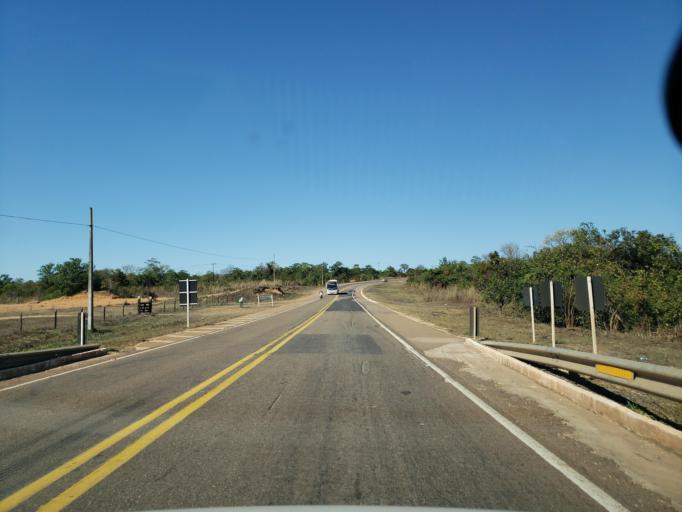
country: BR
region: Mato Grosso
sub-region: Poxoreo
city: Poxoreo
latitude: -15.7766
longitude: -54.3676
